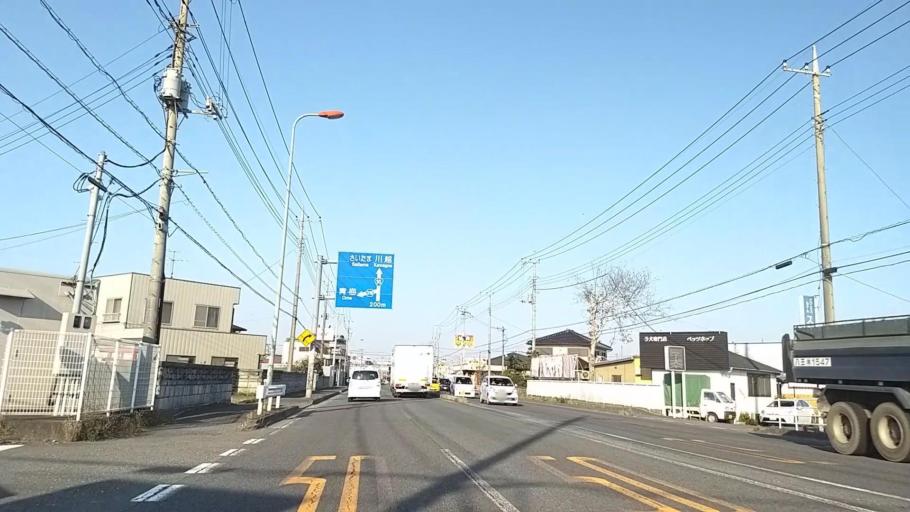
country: JP
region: Saitama
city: Sayama
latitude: 35.7968
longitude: 139.3664
